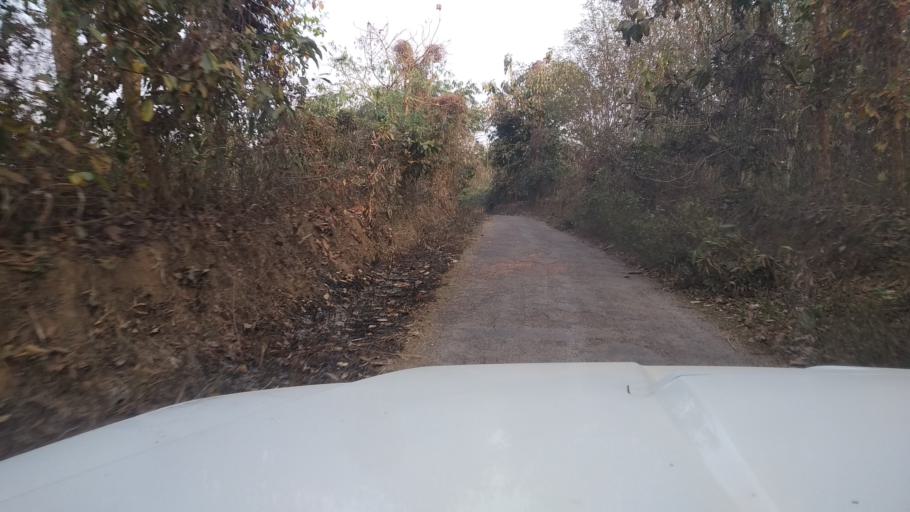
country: IN
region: Tripura
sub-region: South Tripura
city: Belonia
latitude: 23.3187
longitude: 91.3138
